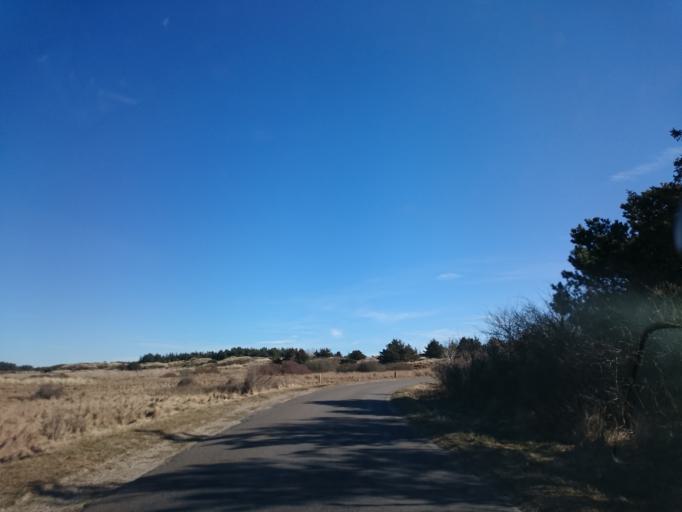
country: DK
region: North Denmark
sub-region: Hjorring Kommune
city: Sindal
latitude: 57.6182
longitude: 10.2798
